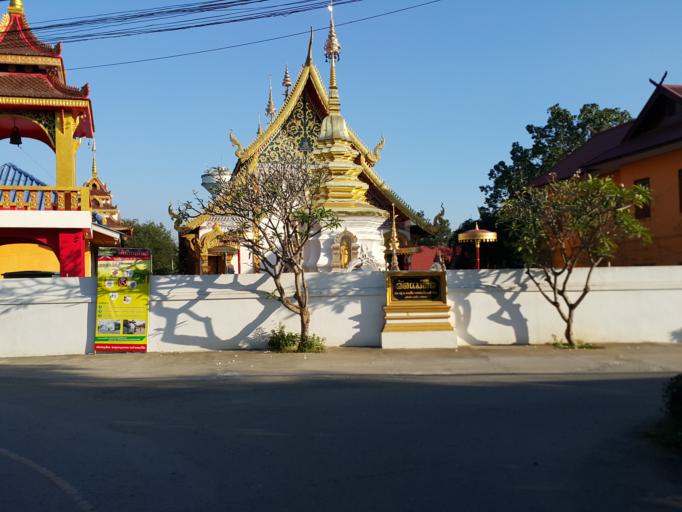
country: TH
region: Chiang Mai
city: San Kamphaeng
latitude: 18.7905
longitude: 99.1088
